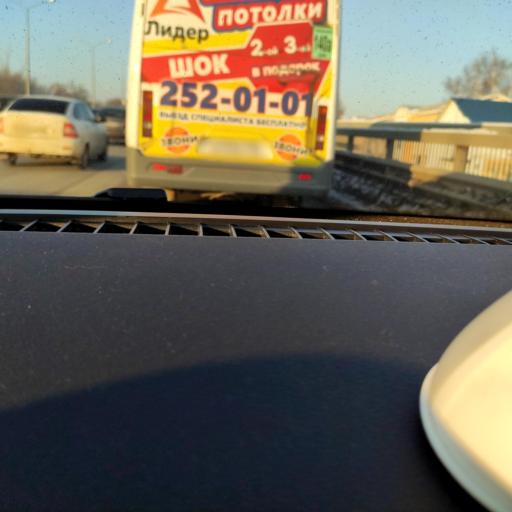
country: RU
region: Samara
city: Samara
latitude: 53.1698
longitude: 50.1923
